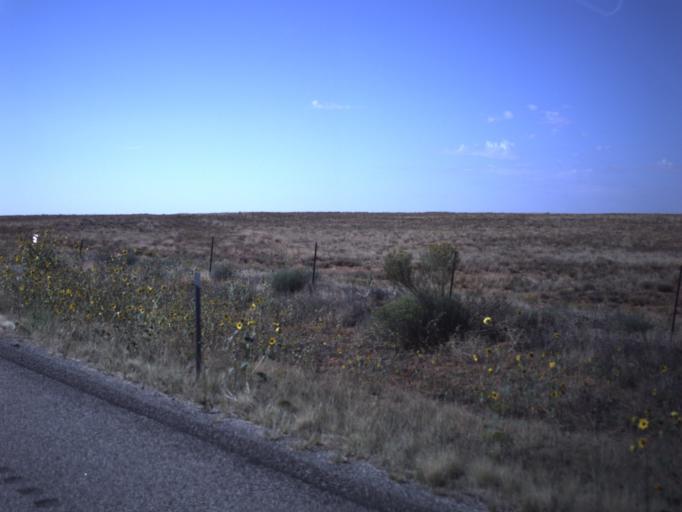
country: US
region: Utah
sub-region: San Juan County
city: Blanding
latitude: 37.4504
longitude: -109.4671
